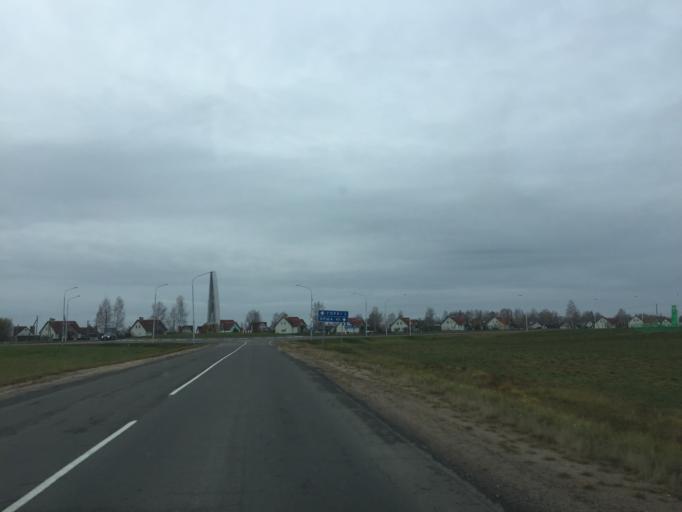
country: BY
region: Mogilev
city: Horki
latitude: 54.3085
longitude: 30.9412
